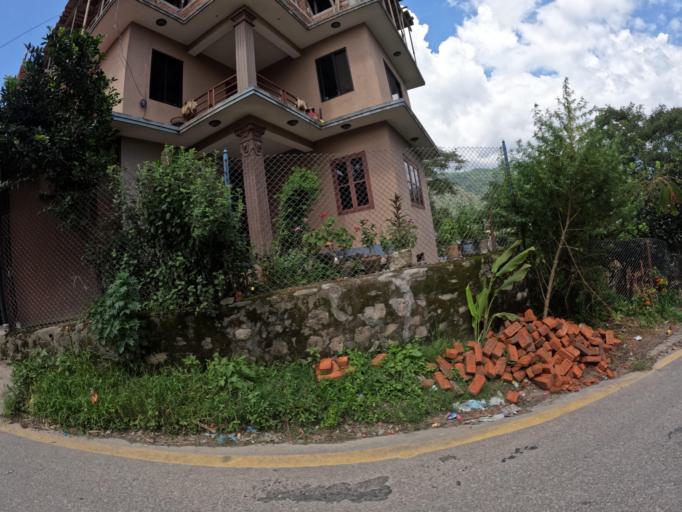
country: NP
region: Central Region
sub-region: Bagmati Zone
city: Kathmandu
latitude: 27.7753
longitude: 85.3282
